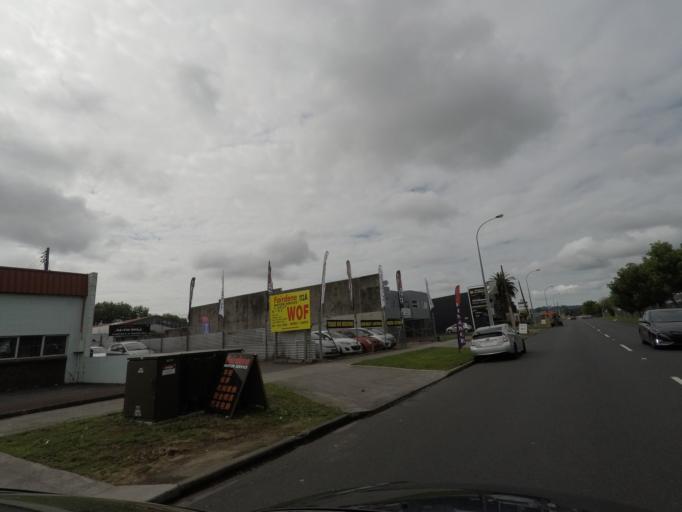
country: NZ
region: Auckland
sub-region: Auckland
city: Waitakere
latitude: -36.8873
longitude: 174.6316
